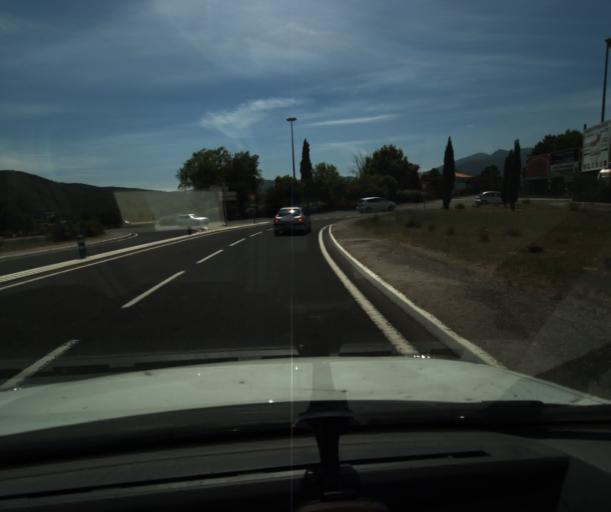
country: FR
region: Languedoc-Roussillon
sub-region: Departement des Pyrenees-Orientales
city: el Volo
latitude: 42.5216
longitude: 2.8223
